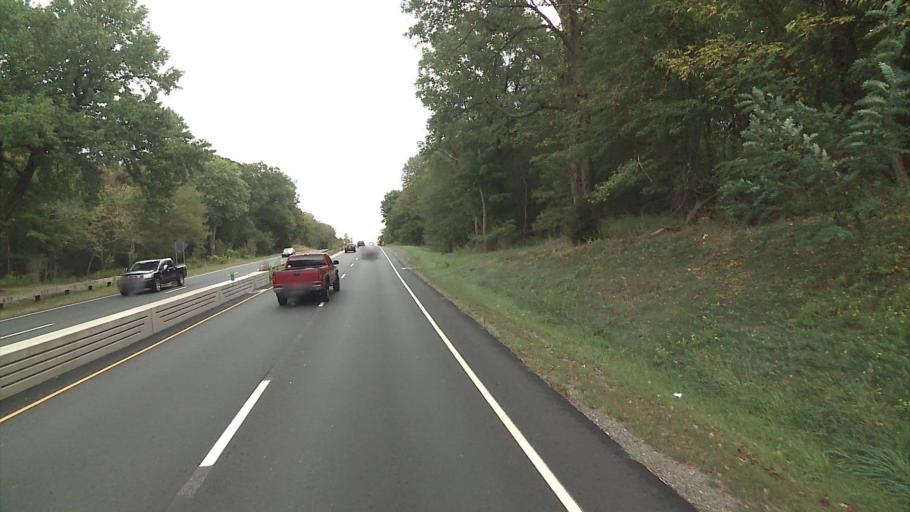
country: US
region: Connecticut
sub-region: Fairfield County
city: North Stamford
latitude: 41.1006
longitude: -73.5819
